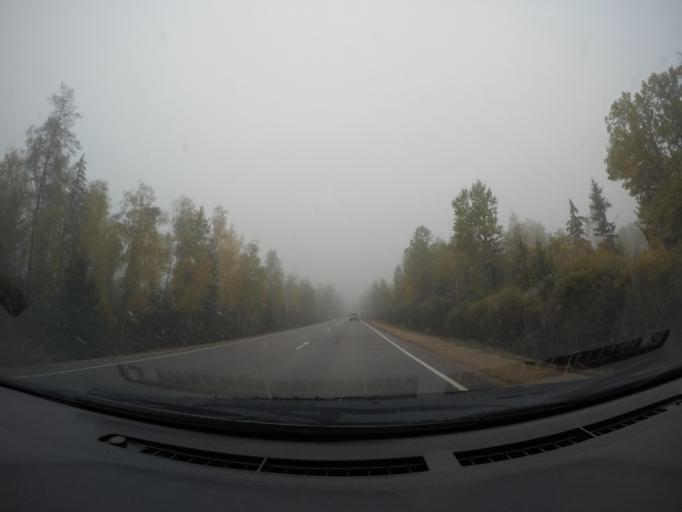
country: RU
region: Moskovskaya
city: Ruza
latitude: 55.7265
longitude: 36.2873
